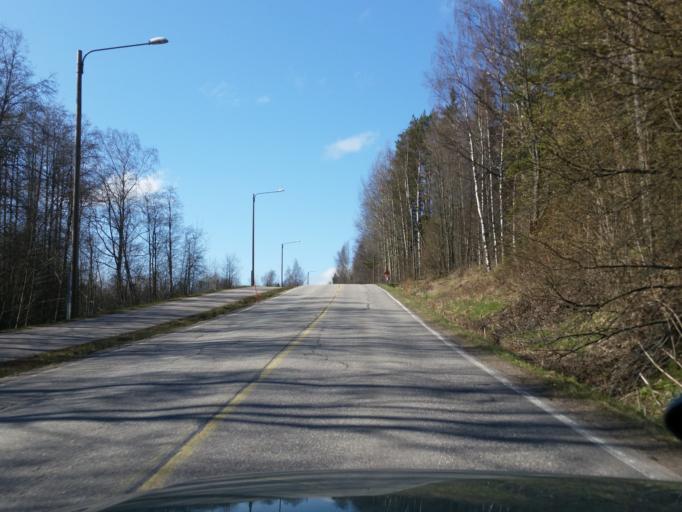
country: FI
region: Uusimaa
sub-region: Helsinki
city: Vihti
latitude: 60.4190
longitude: 24.2780
